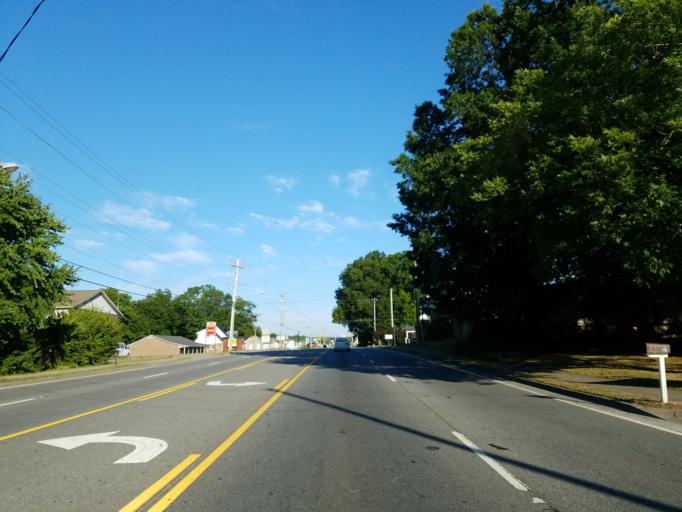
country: US
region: Georgia
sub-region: Gordon County
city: Calhoun
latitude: 34.4834
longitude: -84.9415
